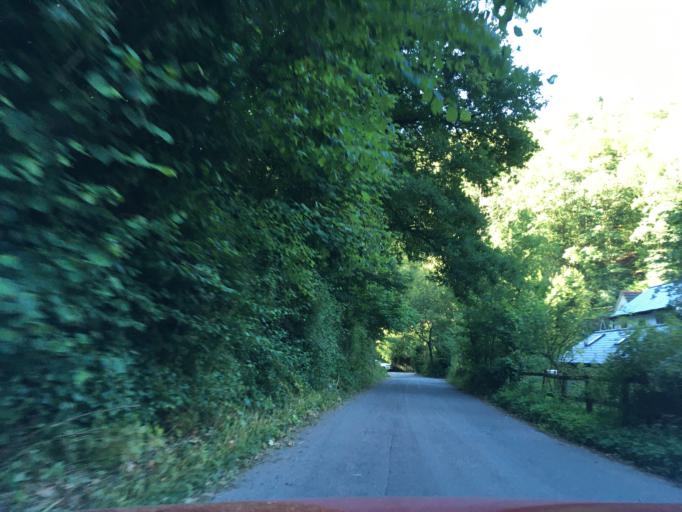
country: GB
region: Wales
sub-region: Monmouthshire
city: Tintern
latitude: 51.6984
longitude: -2.6880
